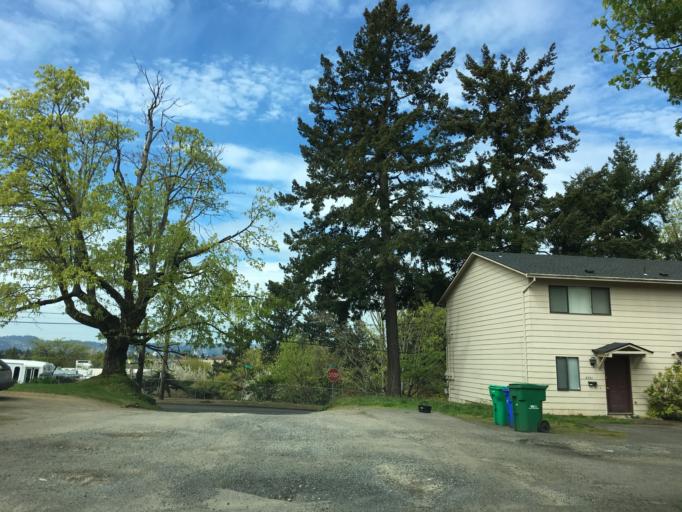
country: US
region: Oregon
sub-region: Multnomah County
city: Lents
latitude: 45.5283
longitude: -122.5938
